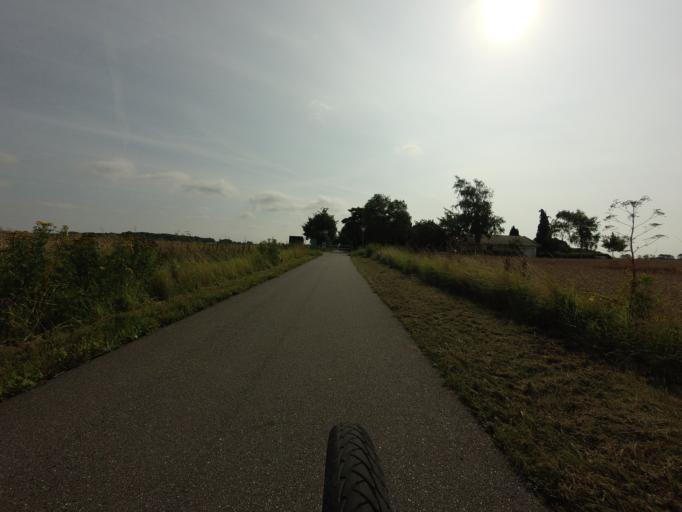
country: DK
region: Zealand
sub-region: Naestved Kommune
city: Naestved
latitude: 55.2564
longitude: 11.6554
